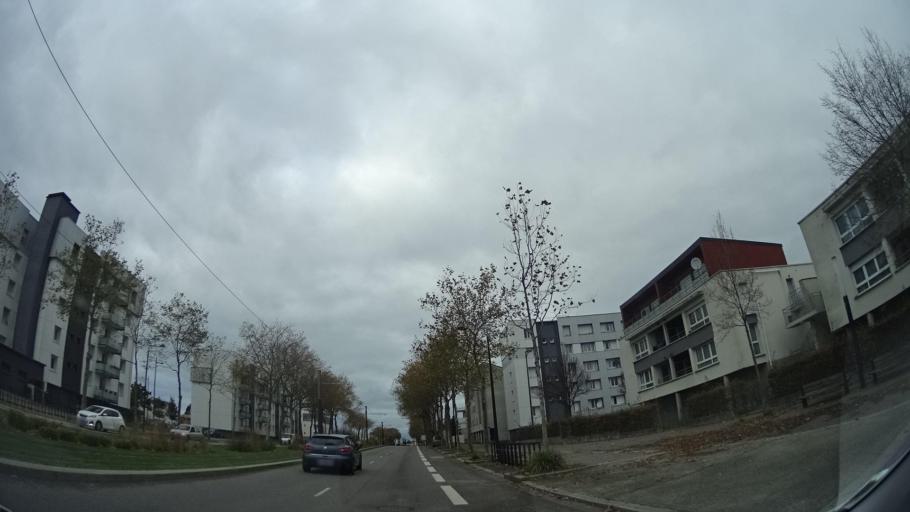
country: FR
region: Haute-Normandie
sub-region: Departement de la Seine-Maritime
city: Le Havre
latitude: 49.5170
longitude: 0.1192
